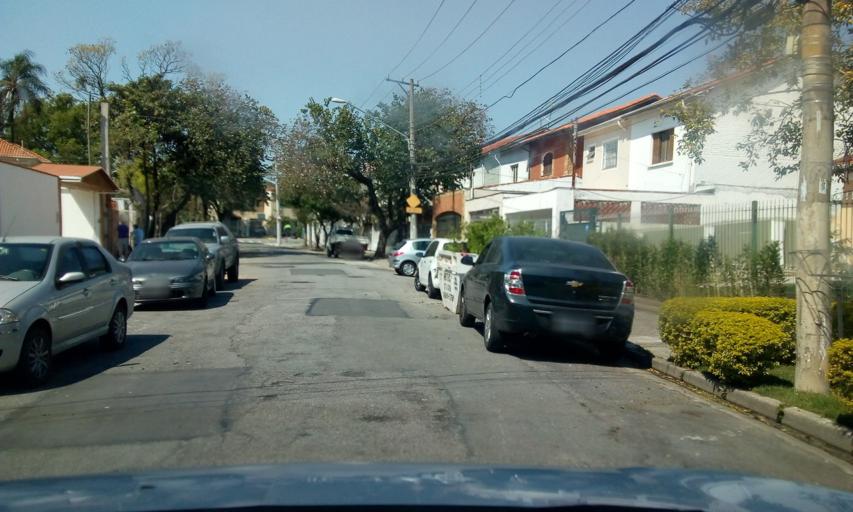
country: BR
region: Sao Paulo
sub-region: Osasco
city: Osasco
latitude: -23.5239
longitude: -46.7146
